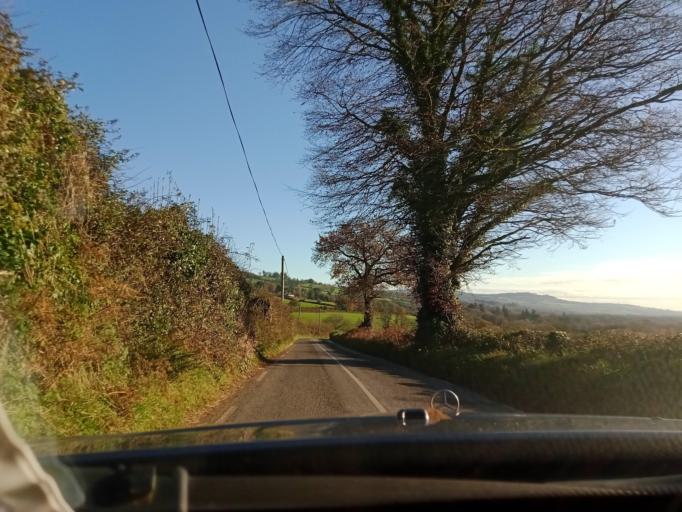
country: IE
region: Leinster
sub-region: Kilkenny
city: Piltown
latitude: 52.3941
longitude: -7.3530
